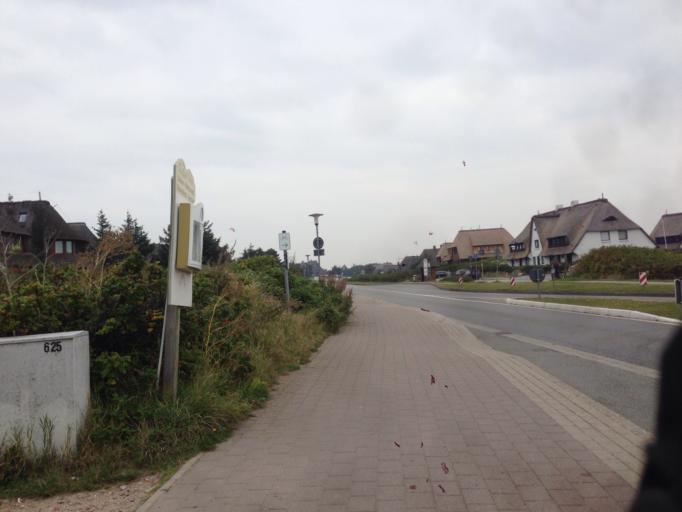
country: DE
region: Schleswig-Holstein
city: Westerland
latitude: 54.8406
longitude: 8.2925
